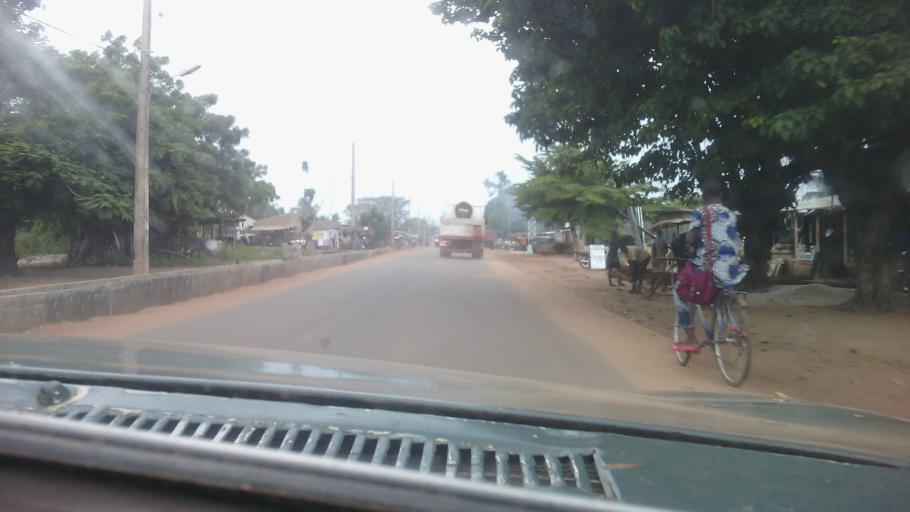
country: BJ
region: Mono
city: Come
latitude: 6.5148
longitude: 1.8239
